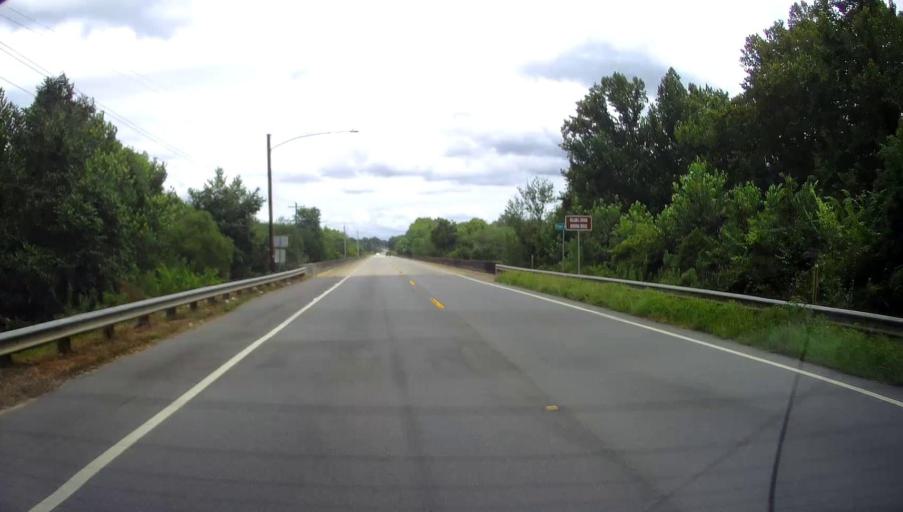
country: US
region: Georgia
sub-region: Macon County
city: Oglethorpe
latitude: 32.2928
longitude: -84.0463
